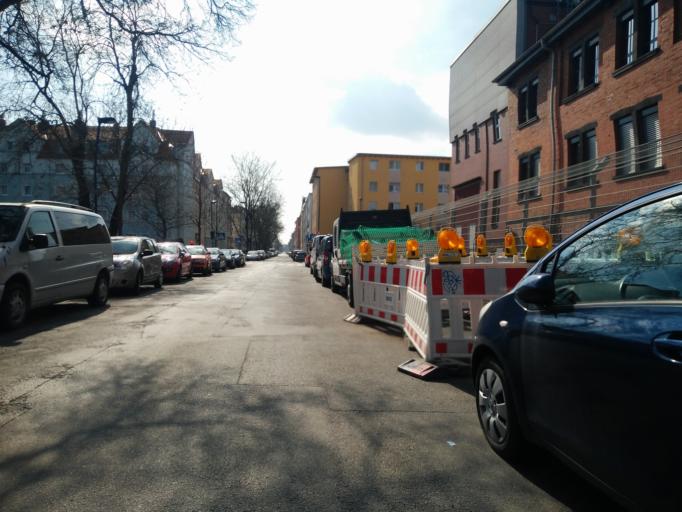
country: DE
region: Hesse
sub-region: Regierungsbezirk Darmstadt
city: Offenbach
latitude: 50.1110
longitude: 8.7462
